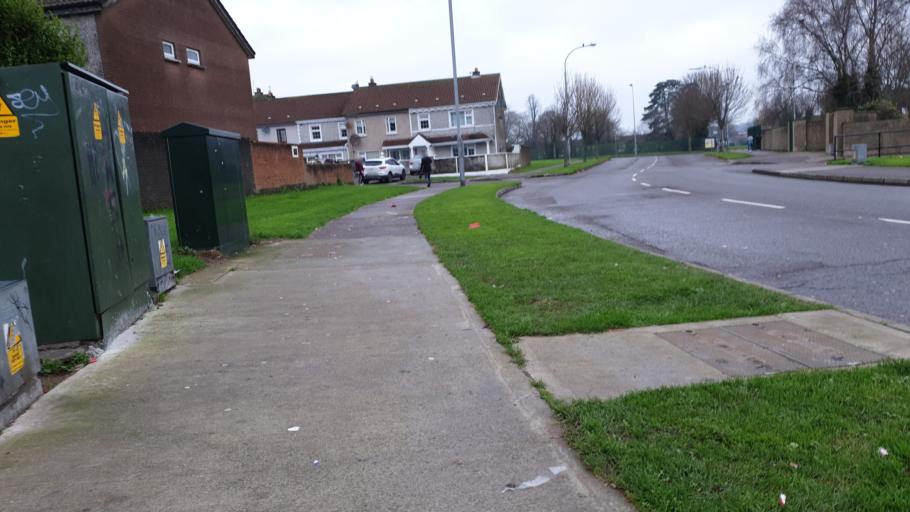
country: IE
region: Munster
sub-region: County Cork
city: Passage West
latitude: 51.8900
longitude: -8.4002
